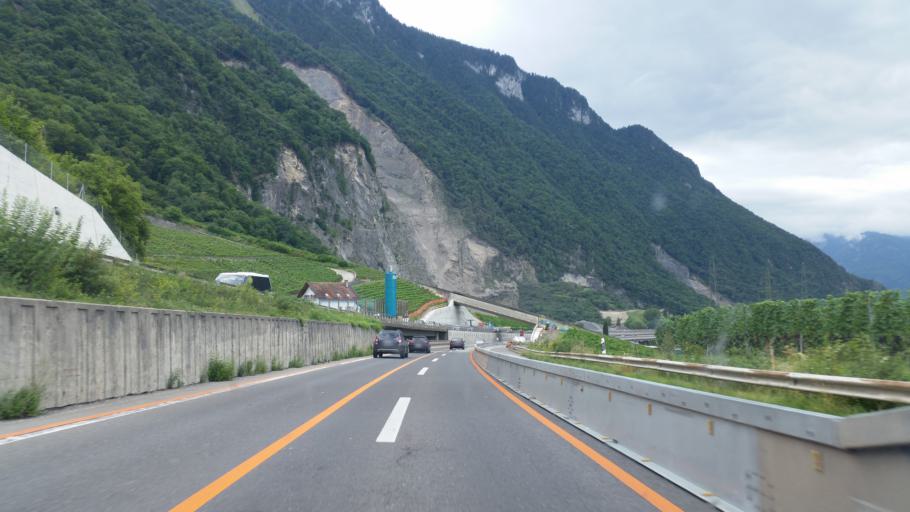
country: CH
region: Vaud
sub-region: Aigle District
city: Villeneuve
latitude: 46.3956
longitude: 6.9373
